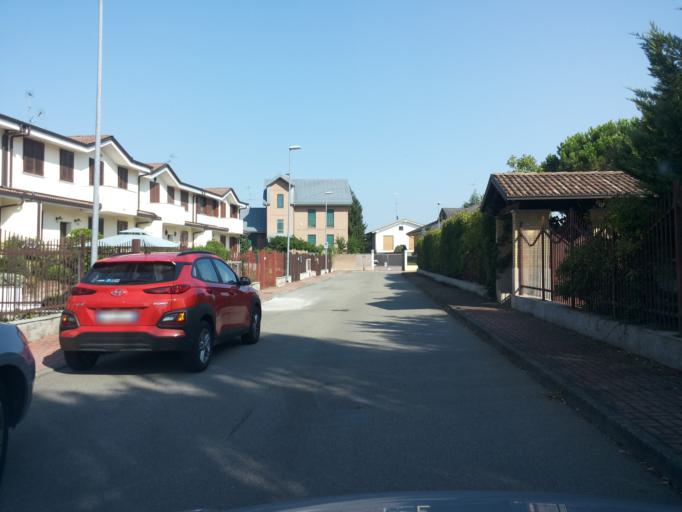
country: IT
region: Piedmont
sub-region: Provincia di Vercelli
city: Caresanablot
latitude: 45.3362
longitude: 8.4014
